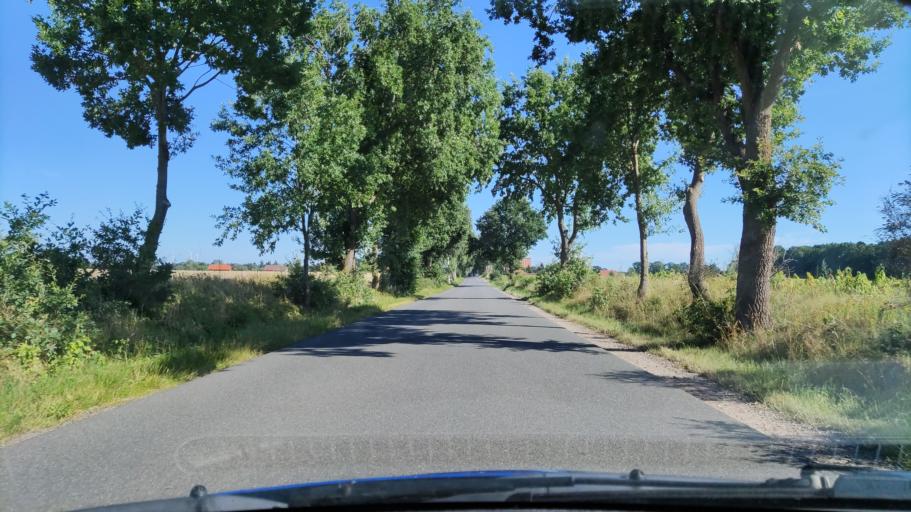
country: DE
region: Lower Saxony
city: Dahlenburg
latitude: 53.1755
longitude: 10.6993
